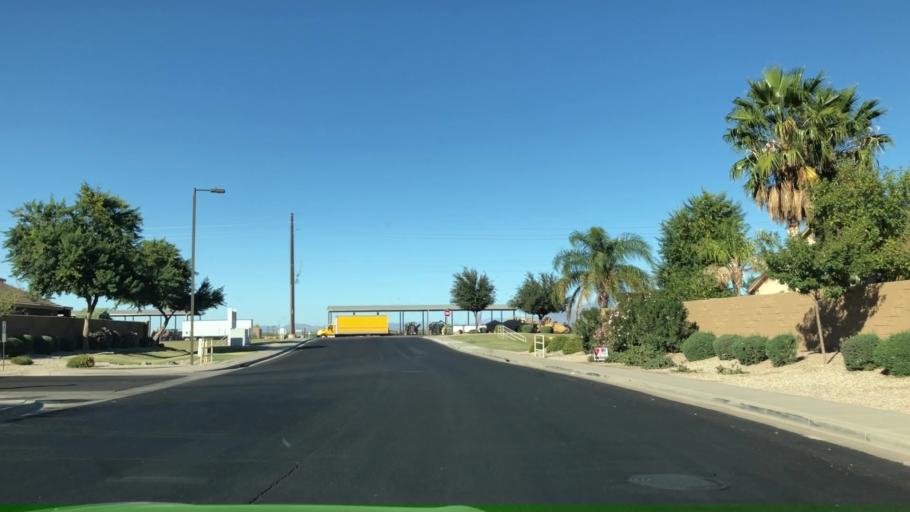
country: US
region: Arizona
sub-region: Pinal County
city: San Tan Valley
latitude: 33.1608
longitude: -111.5361
